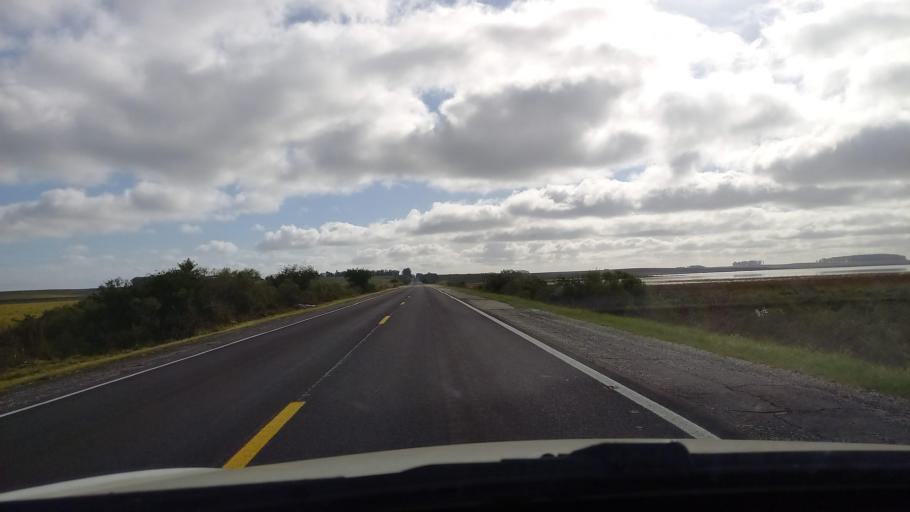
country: BR
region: Rio Grande do Sul
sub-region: Dom Pedrito
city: Dom Pedrito
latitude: -30.8875
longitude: -54.8694
